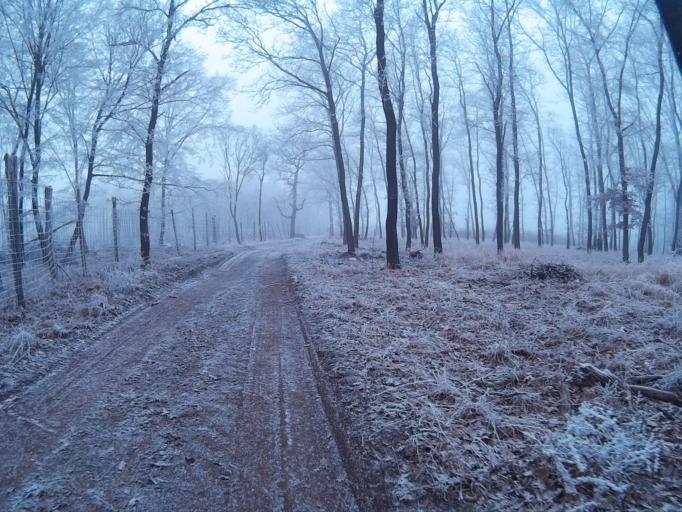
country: HU
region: Komarom-Esztergom
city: Oroszlany
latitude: 47.4409
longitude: 18.3749
